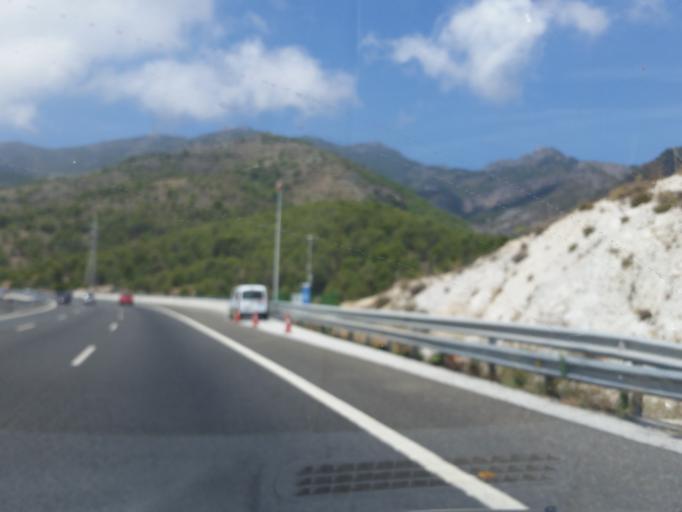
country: ES
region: Andalusia
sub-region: Provincia de Malaga
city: Benalmadena
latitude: 36.6051
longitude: -4.5641
